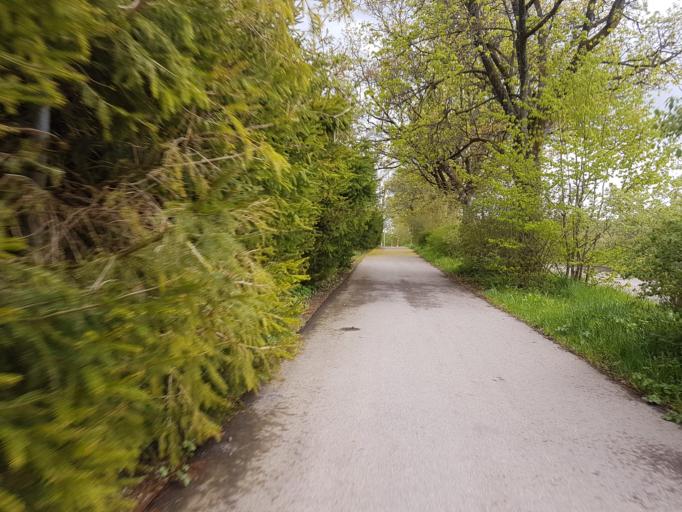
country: DE
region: Baden-Wuerttemberg
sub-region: Freiburg Region
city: Bad Durrheim
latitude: 48.0495
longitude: 8.5280
